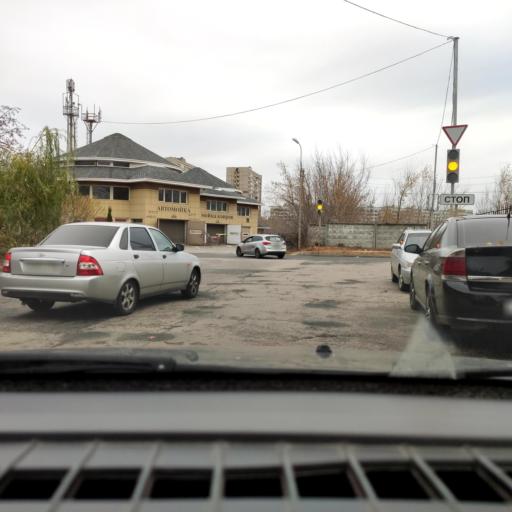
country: RU
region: Samara
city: Tol'yatti
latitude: 53.5234
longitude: 49.3296
